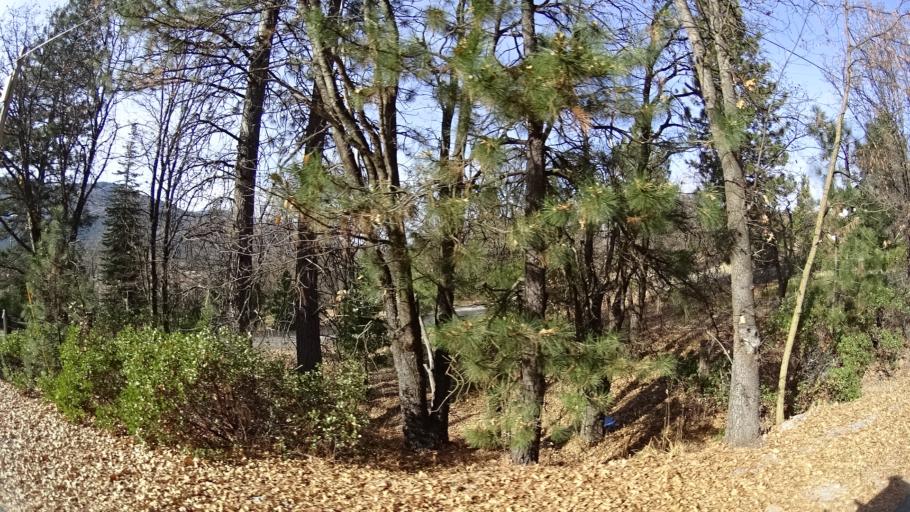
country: US
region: California
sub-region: Siskiyou County
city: Weed
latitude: 41.4027
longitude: -122.4166
